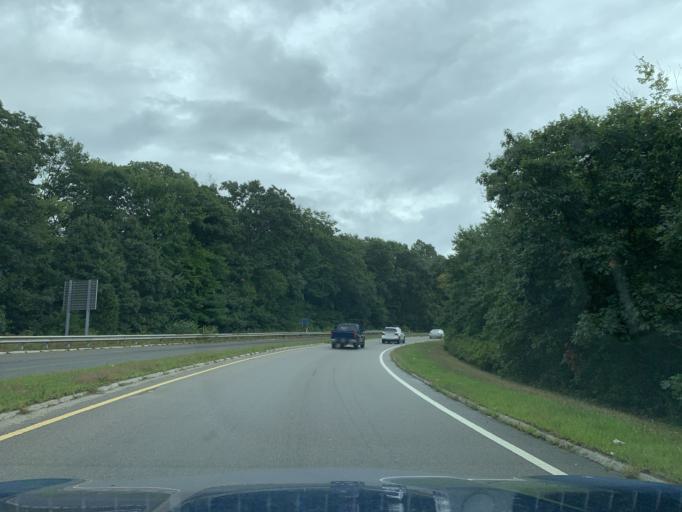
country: US
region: Rhode Island
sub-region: Bristol County
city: Warren
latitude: 41.7759
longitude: -71.2596
